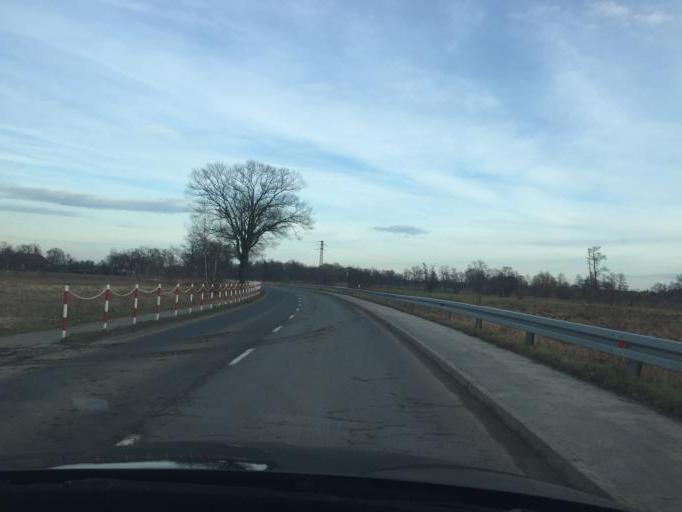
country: PL
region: Lubusz
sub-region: Powiat zarski
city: Brody
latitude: 51.7841
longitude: 14.7740
